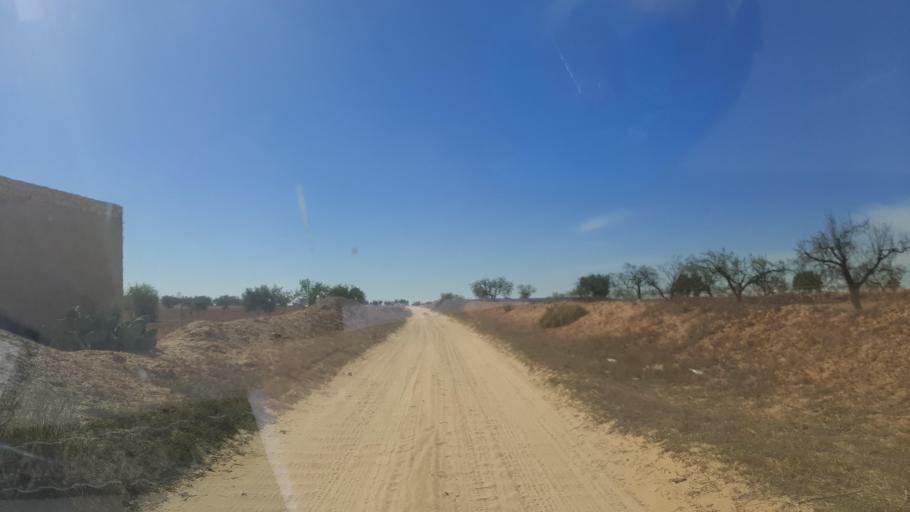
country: TN
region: Safaqis
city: Sfax
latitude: 34.8153
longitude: 10.5486
